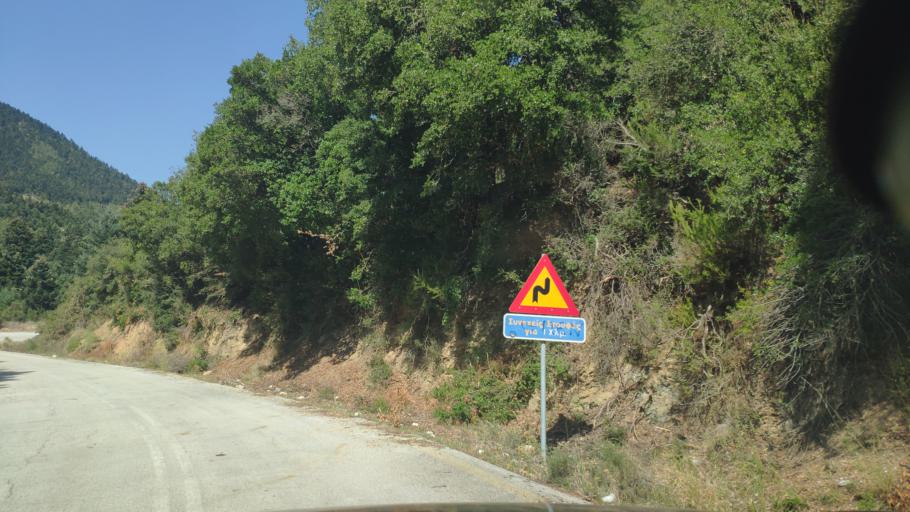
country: GR
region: Peloponnese
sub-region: Nomos Korinthias
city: Nemea
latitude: 37.8588
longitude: 22.3831
